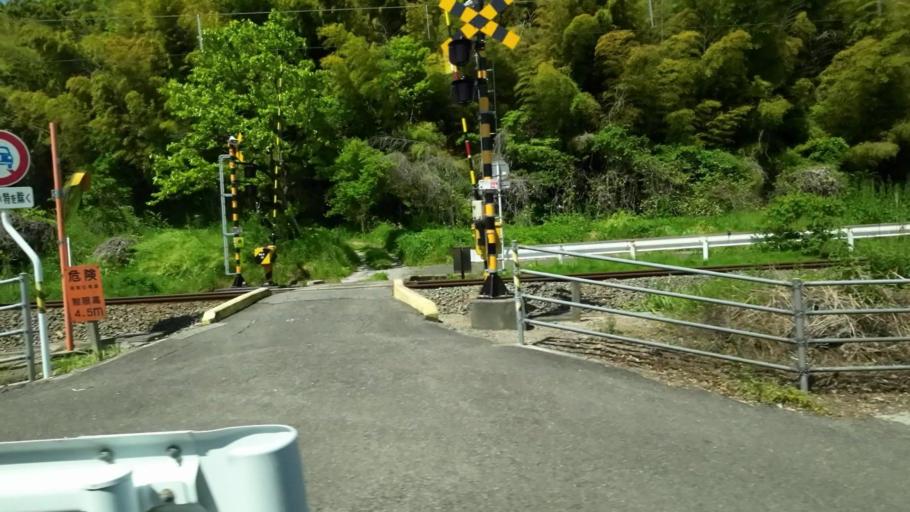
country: JP
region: Ehime
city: Hojo
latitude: 34.0775
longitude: 132.9854
